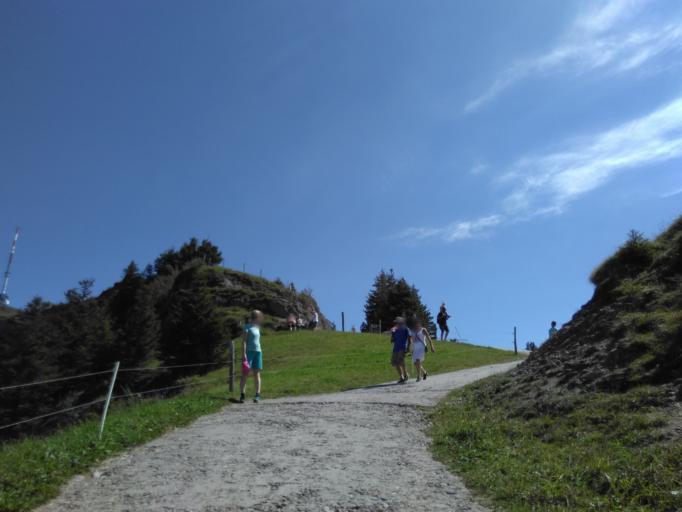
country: CH
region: Lucerne
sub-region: Lucerne-Land District
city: Vitznau
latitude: 47.0550
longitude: 8.4767
